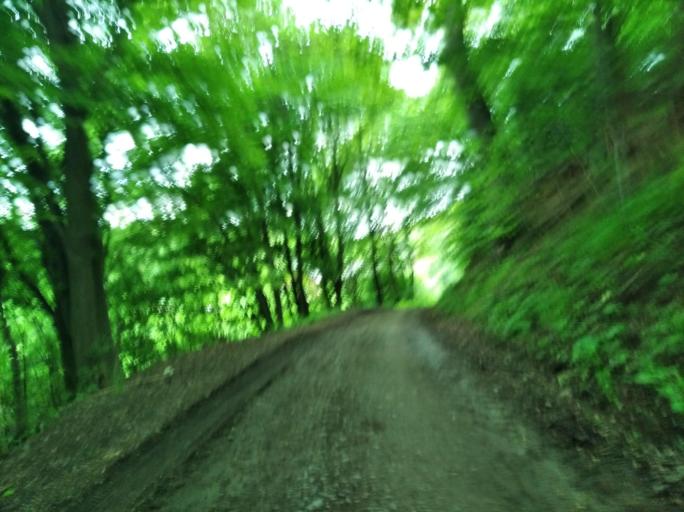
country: PL
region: Subcarpathian Voivodeship
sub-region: Powiat brzozowski
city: Jasionow
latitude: 49.6690
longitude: 21.9867
